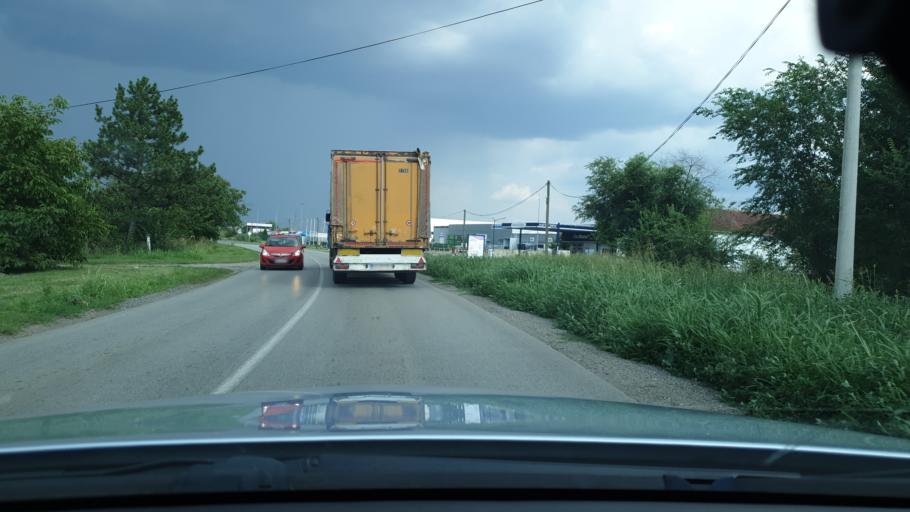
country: RS
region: Autonomna Pokrajina Vojvodina
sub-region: Srednjebanatski Okrug
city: Zrenjanin
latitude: 45.3827
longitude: 20.4315
